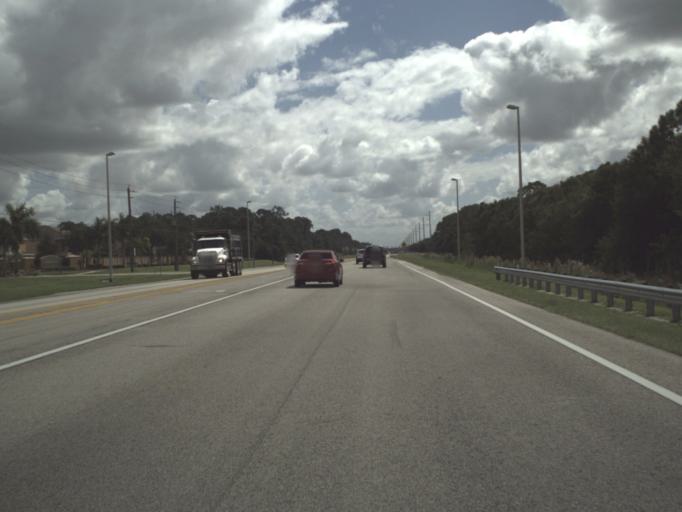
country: US
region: Florida
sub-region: Lee County
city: Gateway
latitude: 26.6147
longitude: -81.7635
